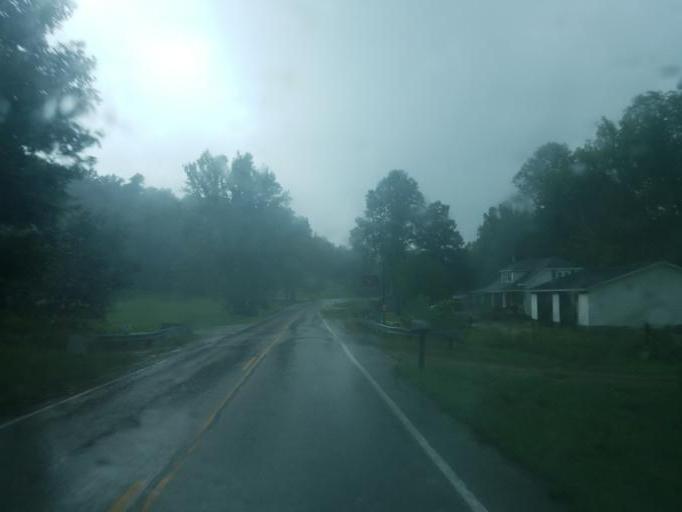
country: US
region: Kentucky
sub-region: Carter County
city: Olive Hill
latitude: 38.2821
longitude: -83.3021
